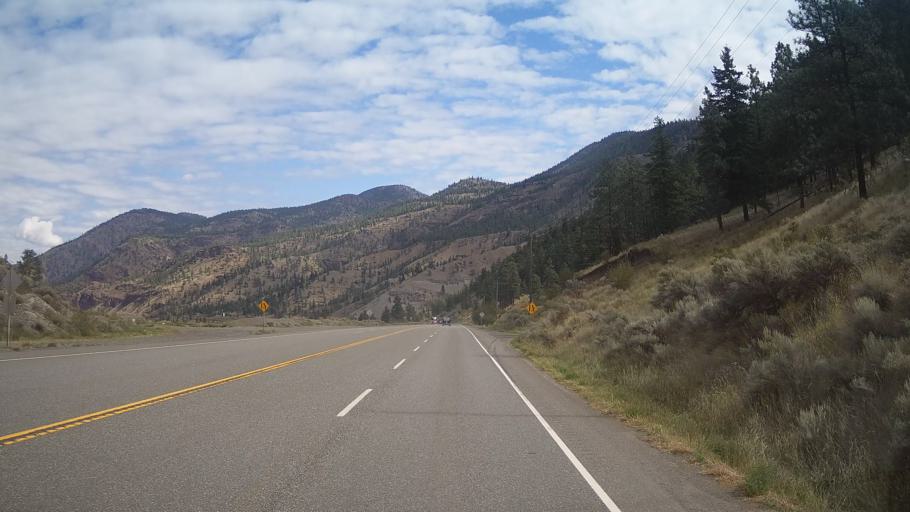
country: CA
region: British Columbia
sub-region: Thompson-Nicola Regional District
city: Ashcroft
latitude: 50.2867
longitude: -121.4006
